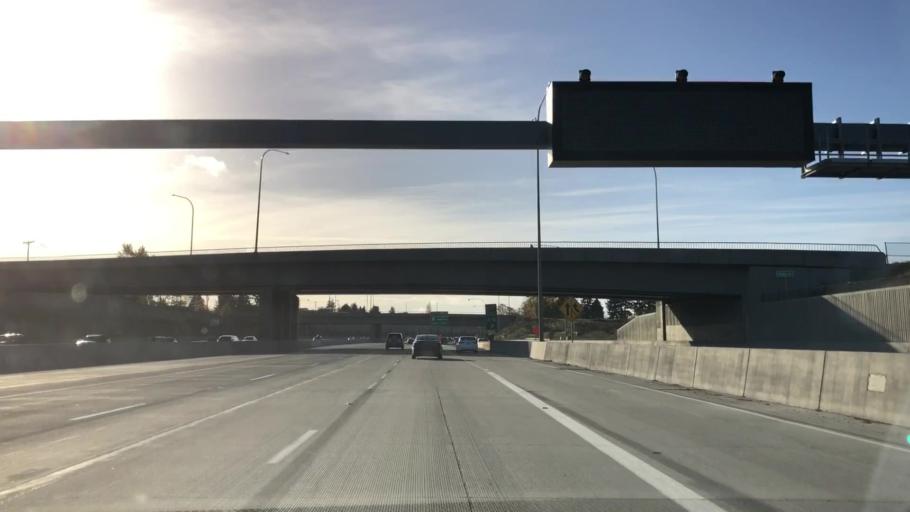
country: US
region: Washington
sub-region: Pierce County
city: Tacoma
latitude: 47.2320
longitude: -122.4398
